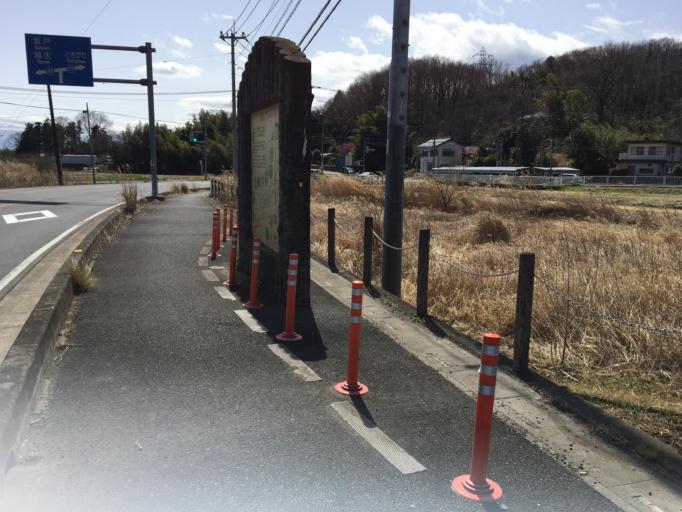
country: JP
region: Saitama
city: Morohongo
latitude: 35.9943
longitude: 139.3339
